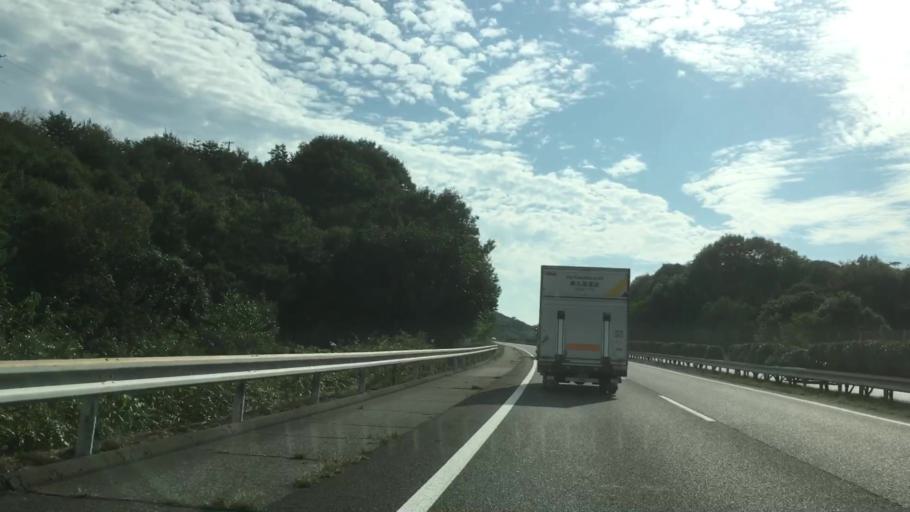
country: JP
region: Yamaguchi
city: Yanai
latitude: 34.0769
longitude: 132.0701
